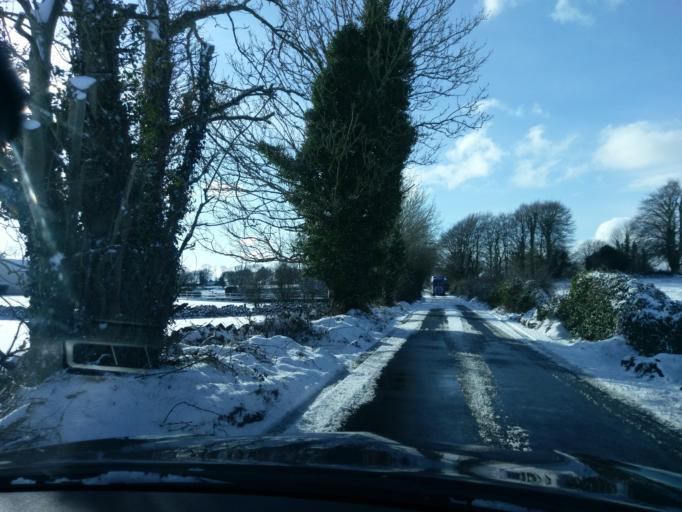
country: IE
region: Connaught
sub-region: County Galway
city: Athenry
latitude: 53.2044
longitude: -8.7800
